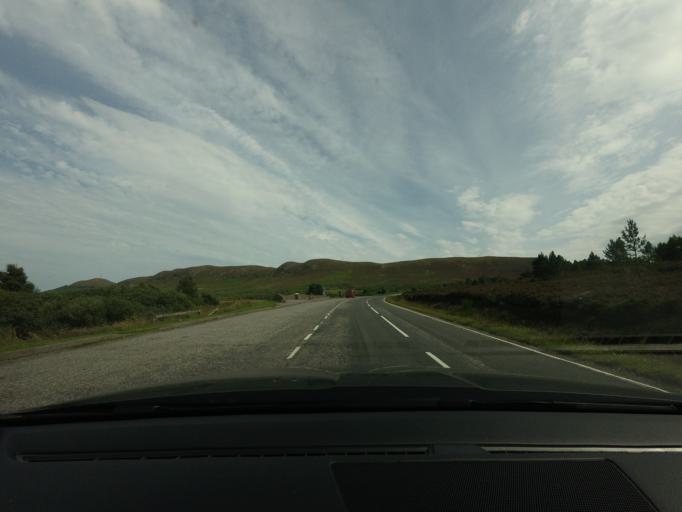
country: GB
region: Scotland
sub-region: Highland
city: Alness
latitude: 57.8413
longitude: -4.2722
